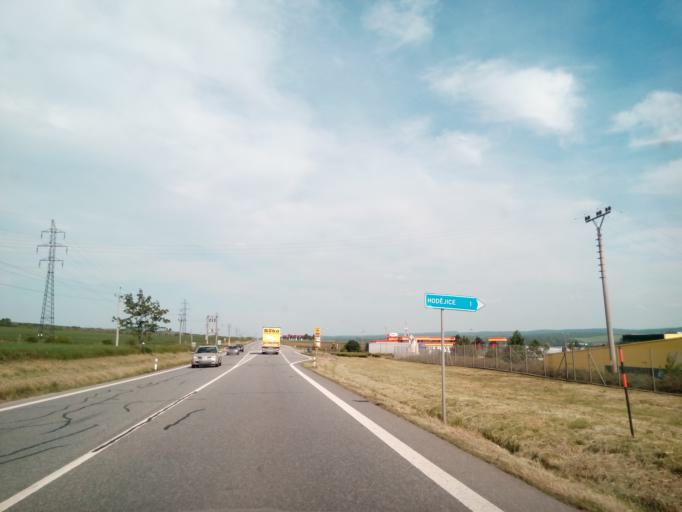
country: CZ
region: South Moravian
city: Slavkov u Brna
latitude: 49.1498
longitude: 16.9135
